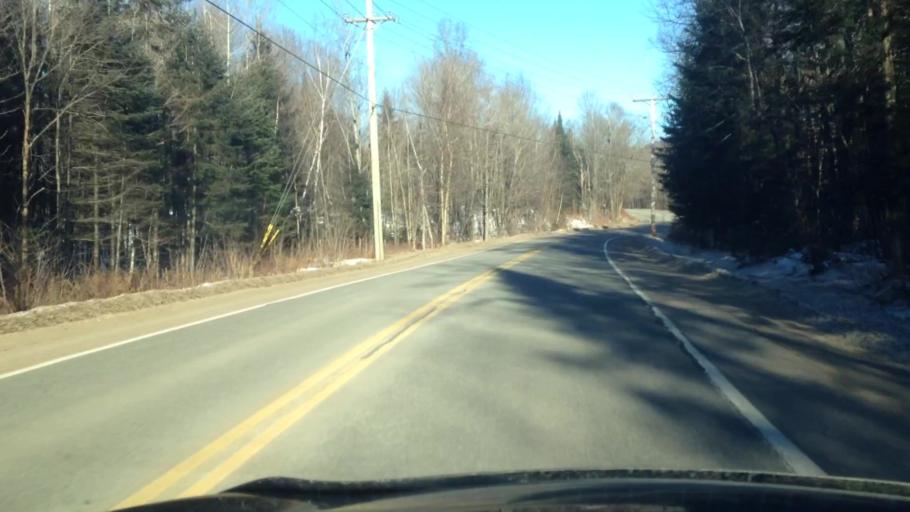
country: CA
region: Quebec
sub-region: Laurentides
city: Mont-Tremblant
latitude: 46.0156
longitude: -74.6140
